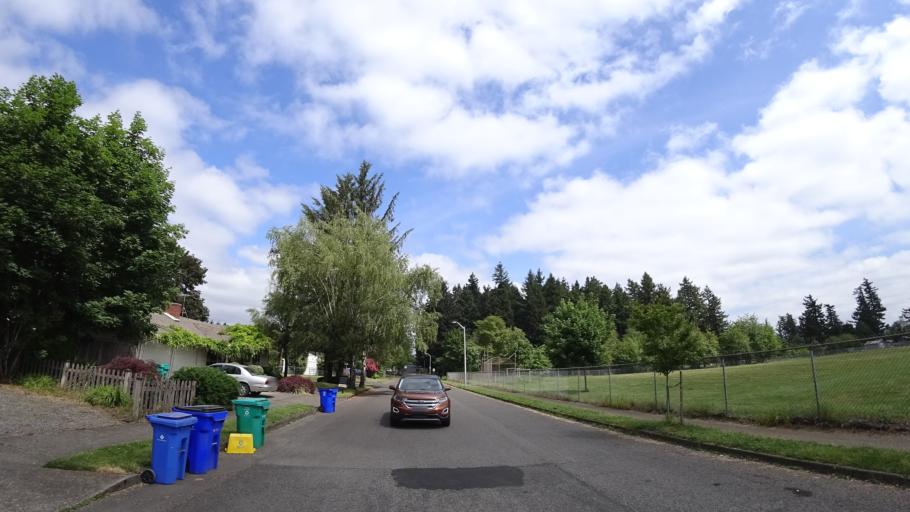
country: US
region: Oregon
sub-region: Multnomah County
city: Gresham
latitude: 45.4967
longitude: -122.4880
